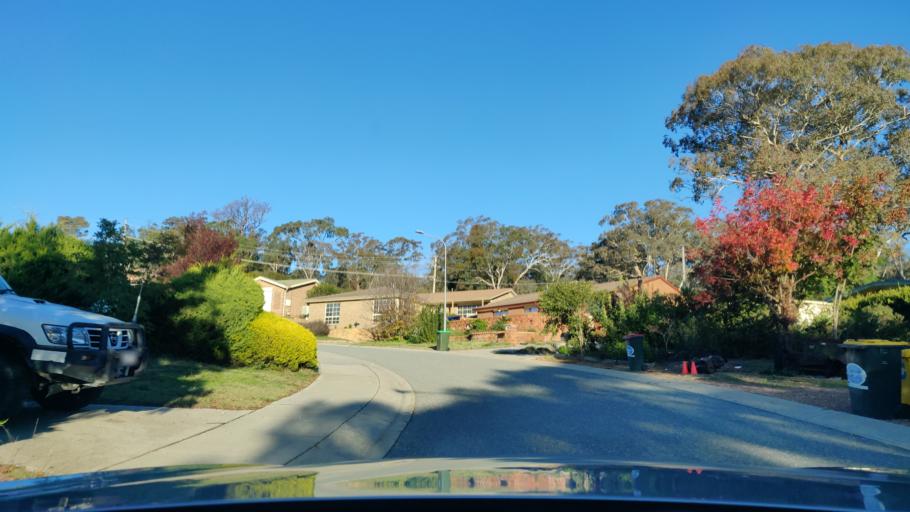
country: AU
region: Australian Capital Territory
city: Macarthur
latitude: -35.4487
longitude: 149.1276
